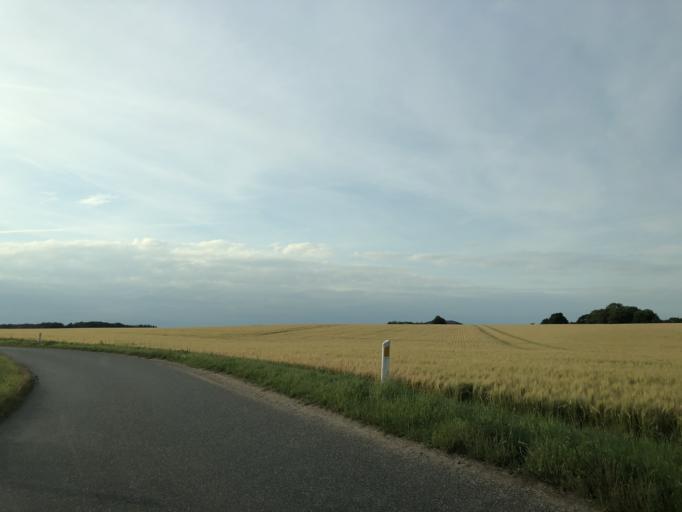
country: DK
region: South Denmark
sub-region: Fredericia Kommune
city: Taulov
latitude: 55.5928
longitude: 9.6154
